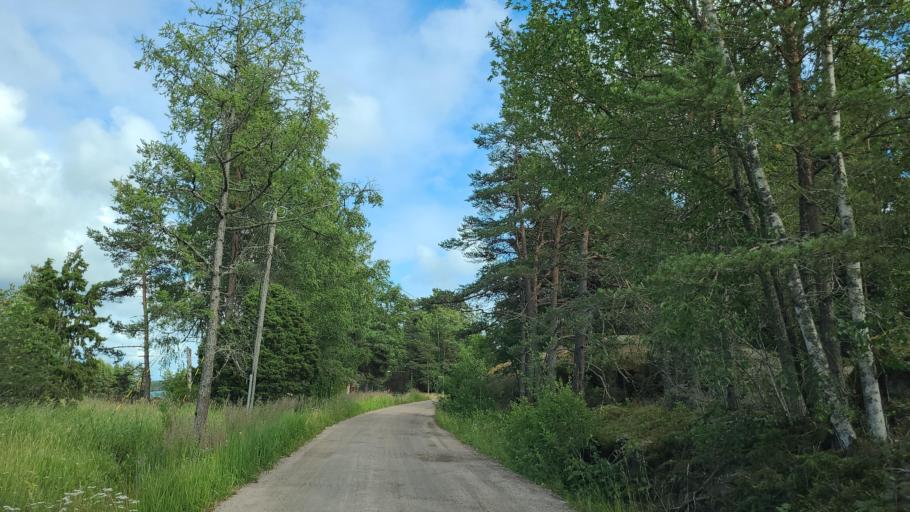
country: FI
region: Varsinais-Suomi
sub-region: Aboland-Turunmaa
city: Nagu
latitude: 60.1398
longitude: 21.8027
